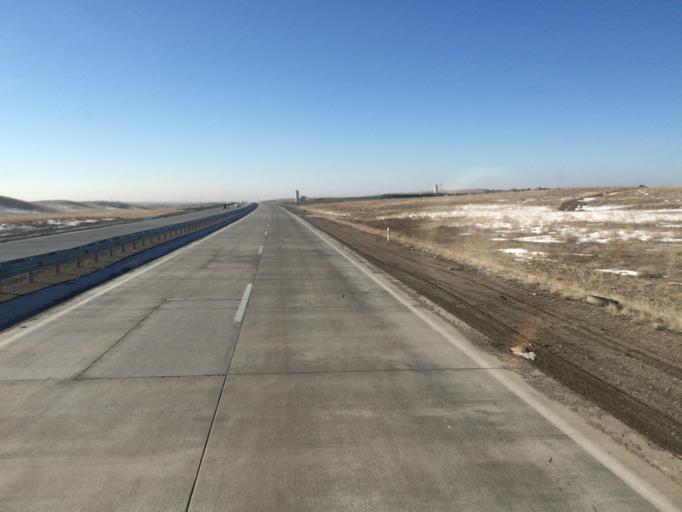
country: KZ
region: Zhambyl
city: Georgiyevka
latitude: 43.3558
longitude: 74.5776
